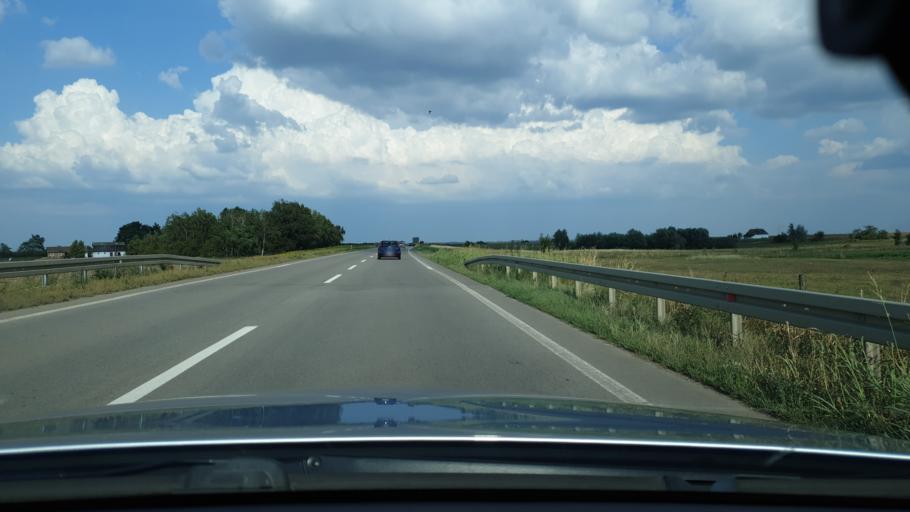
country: RS
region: Autonomna Pokrajina Vojvodina
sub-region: Juznobacki Okrug
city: Zabalj
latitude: 45.3639
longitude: 20.0948
